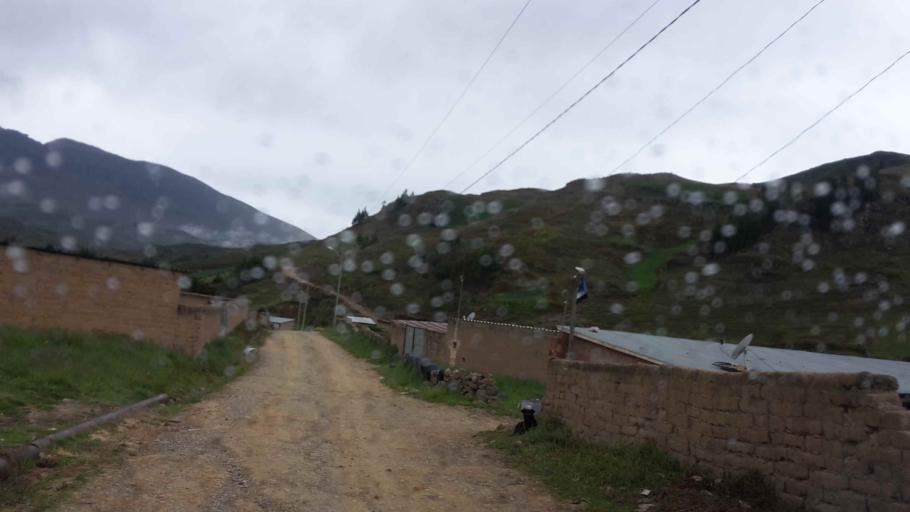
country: BO
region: Cochabamba
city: Cochabamba
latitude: -17.1344
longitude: -66.1049
